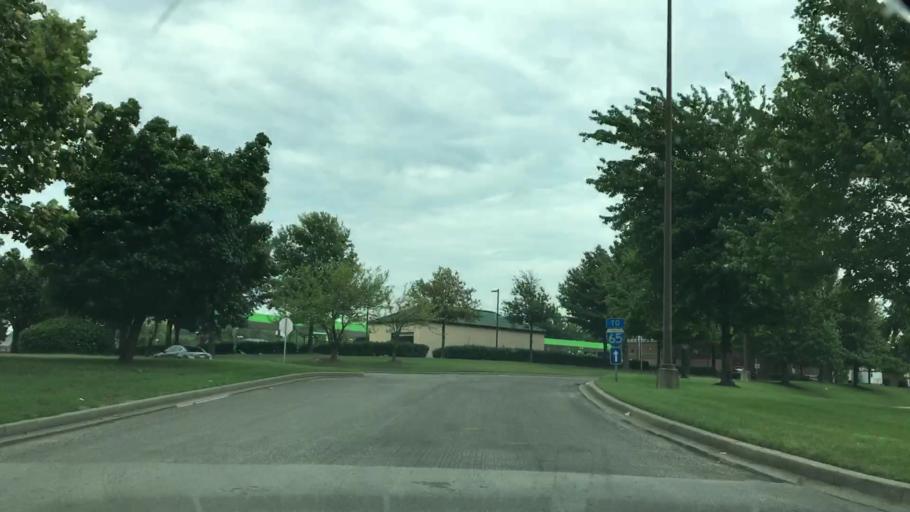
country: US
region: Tennessee
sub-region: Williamson County
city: Brentwood Estates
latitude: 35.9647
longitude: -86.8051
